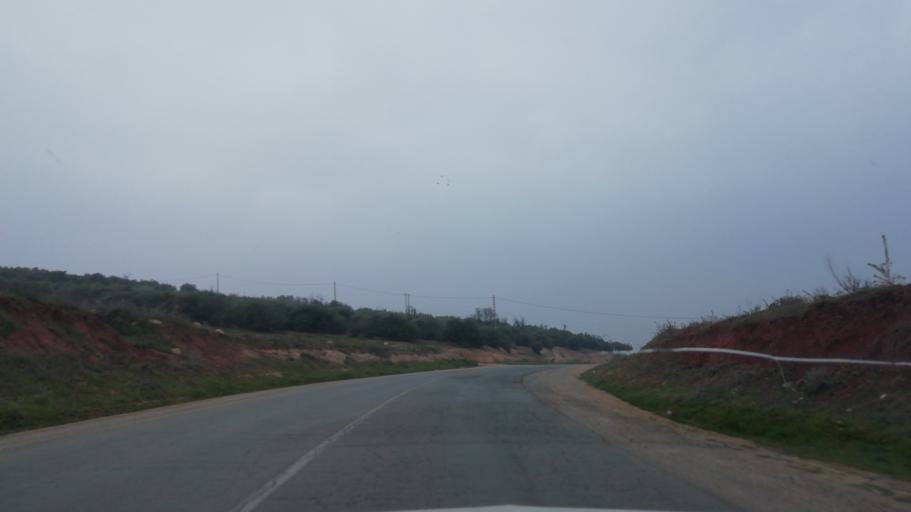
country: DZ
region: Mascara
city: Mascara
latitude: 35.3869
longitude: 0.1622
